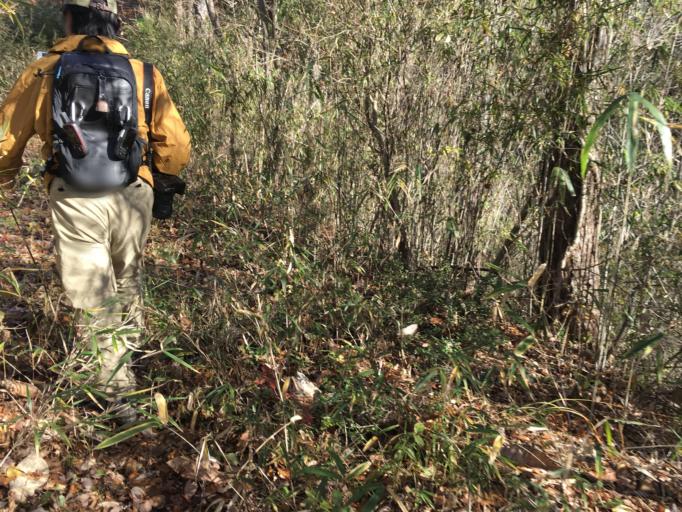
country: JP
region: Iwate
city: Ichinoseki
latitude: 38.8857
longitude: 141.1284
